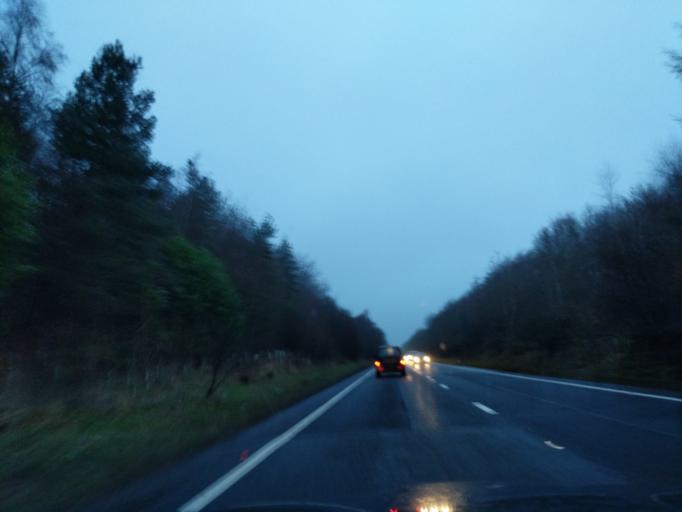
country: GB
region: England
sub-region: Northumberland
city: Felton
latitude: 55.2878
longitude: -1.7273
